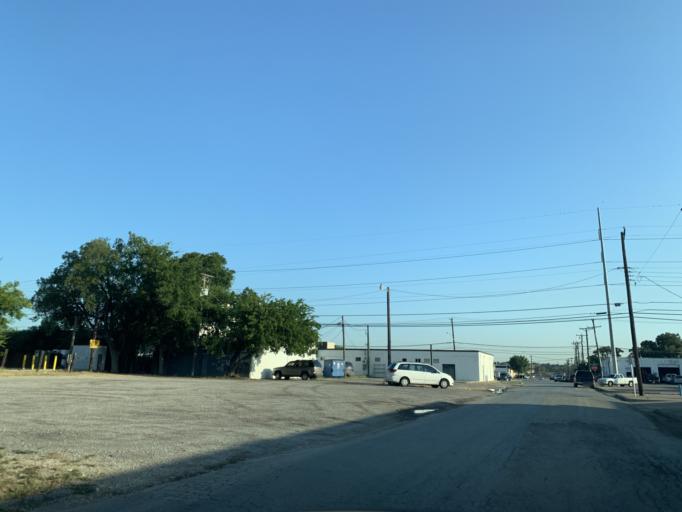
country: US
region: Texas
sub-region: Tarrant County
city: Fort Worth
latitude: 32.7581
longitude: -97.3528
